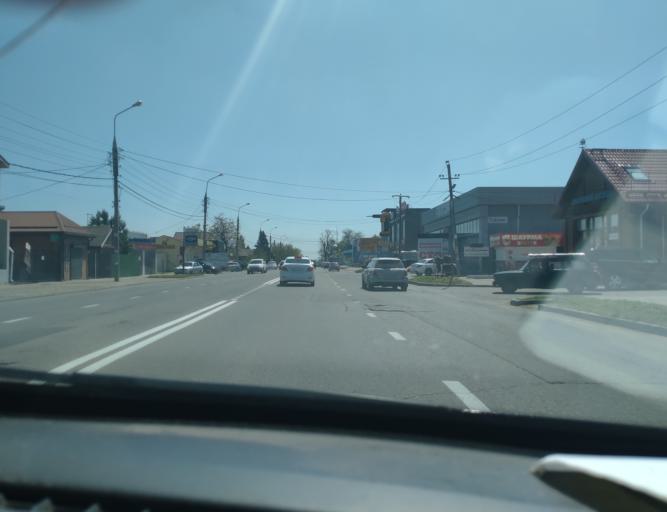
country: RU
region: Krasnodarskiy
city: Krasnodar
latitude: 45.0932
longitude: 39.0138
